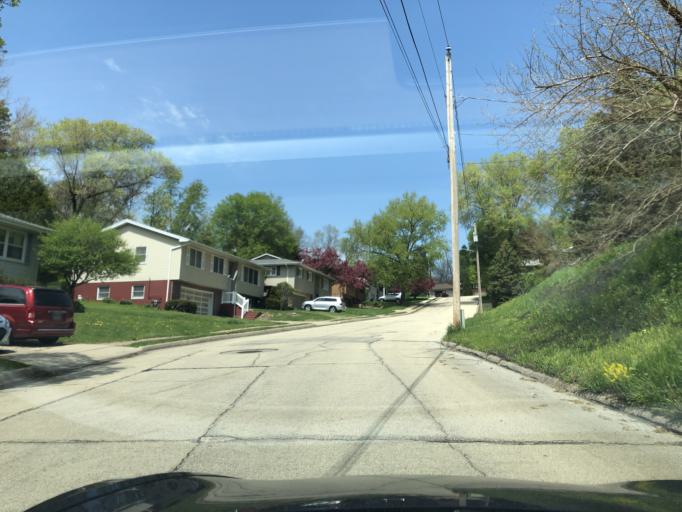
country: US
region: Iowa
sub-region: Dubuque County
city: Dubuque
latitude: 42.4830
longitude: -90.6698
